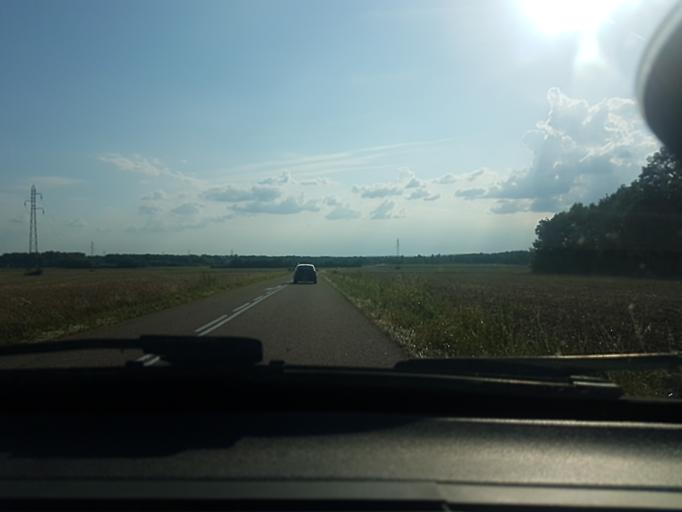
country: FR
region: Bourgogne
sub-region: Departement de Saone-et-Loire
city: Varennes-le-Grand
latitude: 46.7043
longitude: 4.8571
